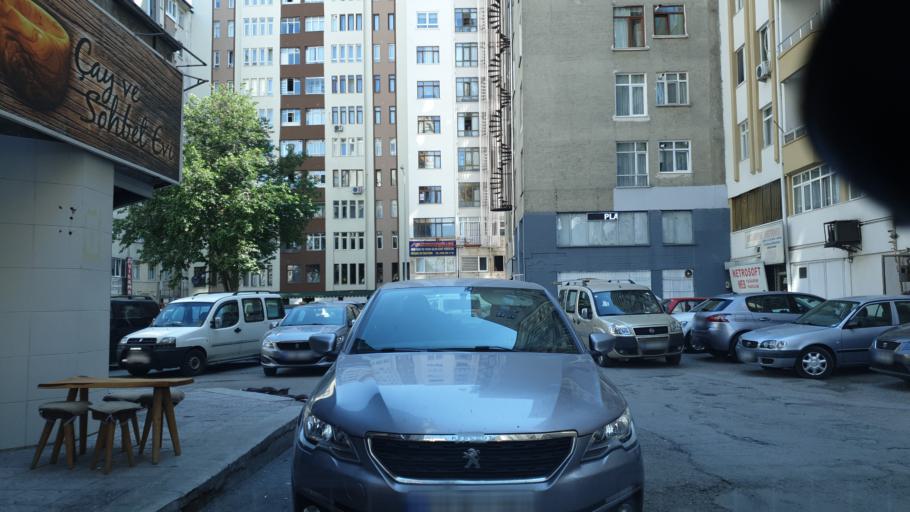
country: TR
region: Kayseri
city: Kayseri
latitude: 38.7255
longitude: 35.4944
